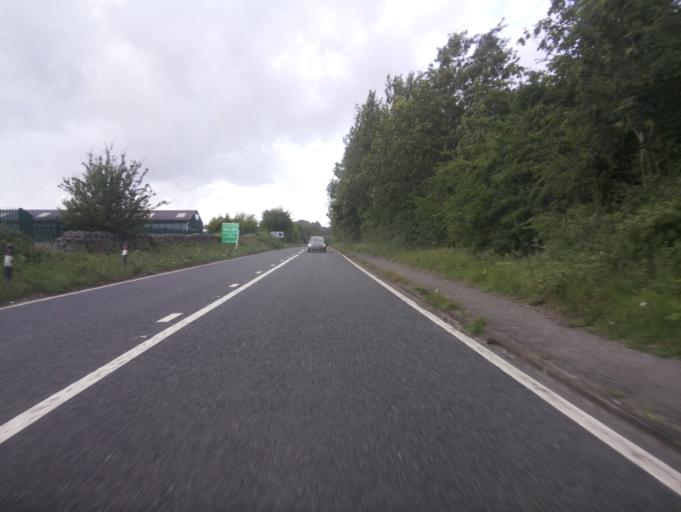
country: GB
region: England
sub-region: Gloucestershire
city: Shipton Village
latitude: 51.8716
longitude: -1.9641
